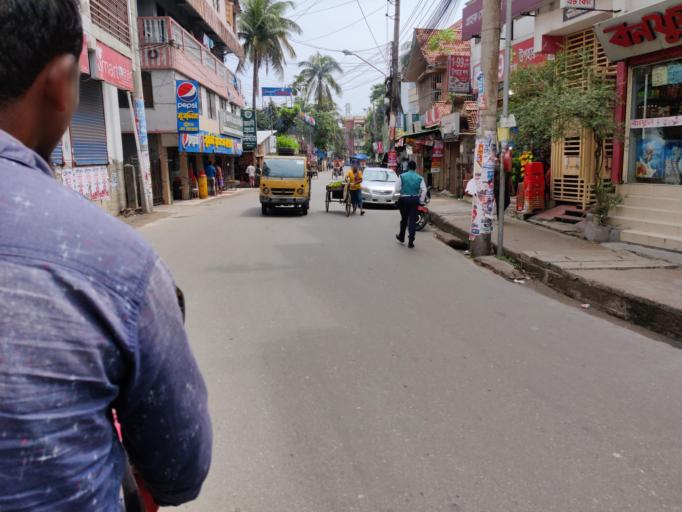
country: BD
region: Barisal
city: Barisal
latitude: 22.7015
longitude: 90.3649
